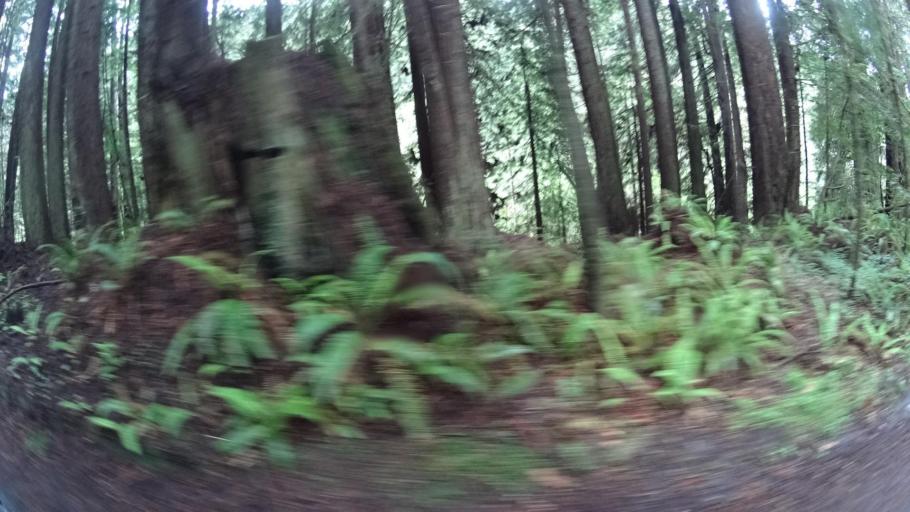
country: US
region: California
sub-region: Humboldt County
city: Bayside
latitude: 40.8192
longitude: -124.0300
